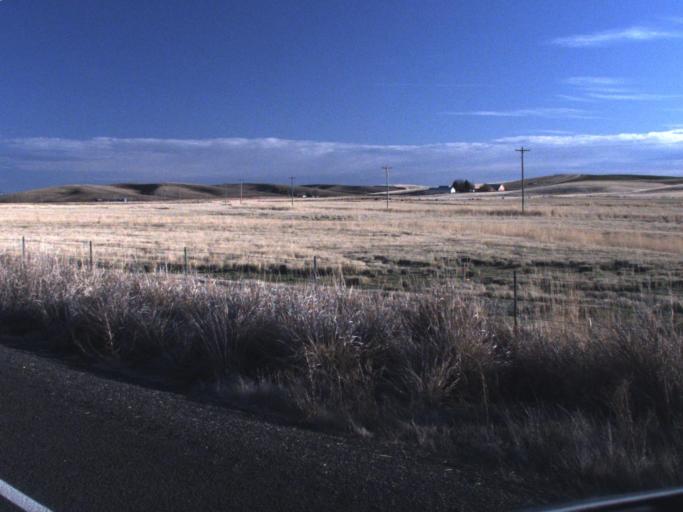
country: US
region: Washington
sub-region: Garfield County
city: Pomeroy
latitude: 46.7620
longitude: -117.7135
